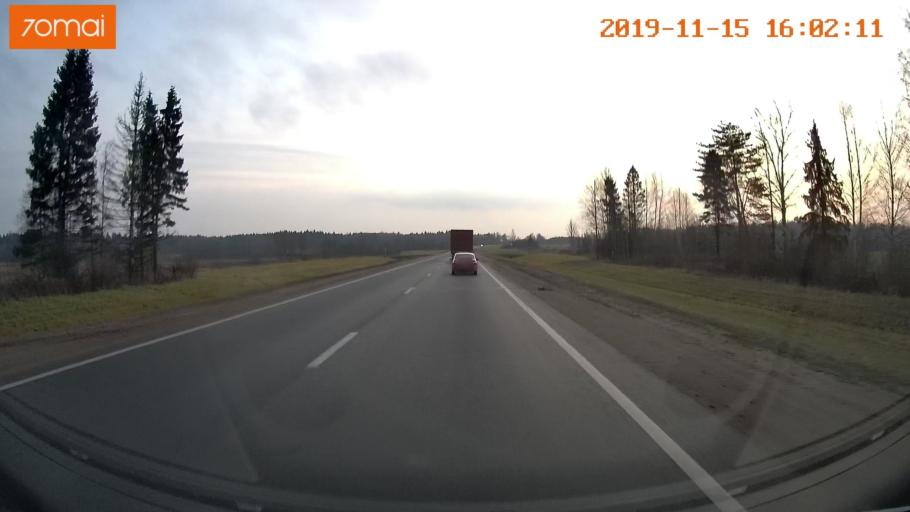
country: RU
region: Jaroslavl
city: Yaroslavl
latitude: 57.7742
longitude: 39.9262
